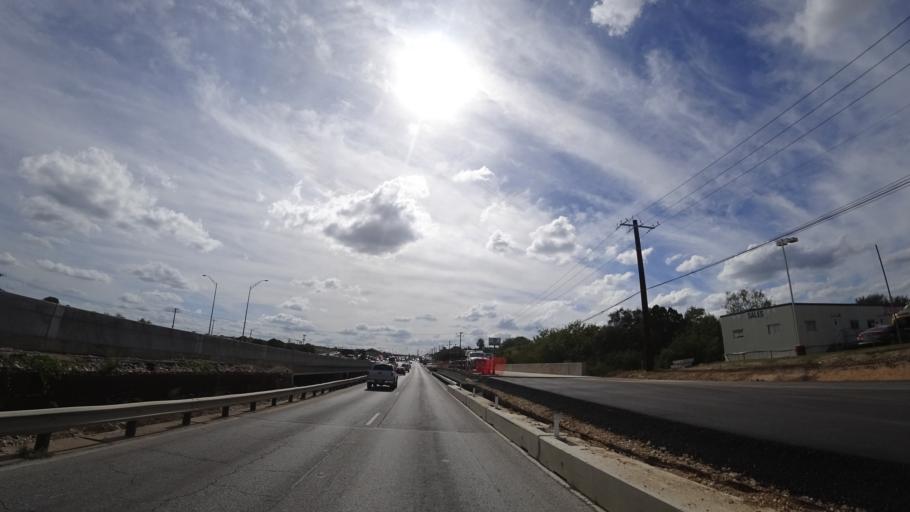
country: US
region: Texas
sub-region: Travis County
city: Austin
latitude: 30.2023
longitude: -97.7615
